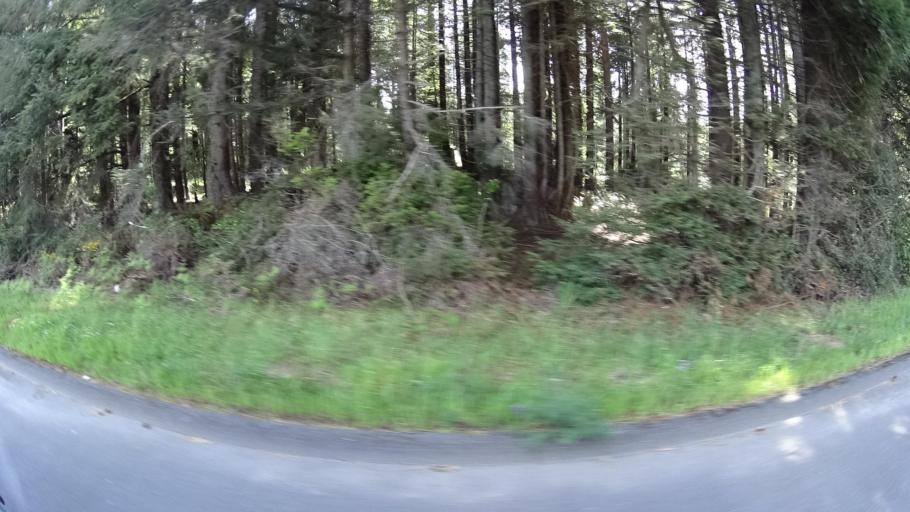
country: US
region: California
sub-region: Humboldt County
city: Cutten
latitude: 40.7565
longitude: -124.1470
